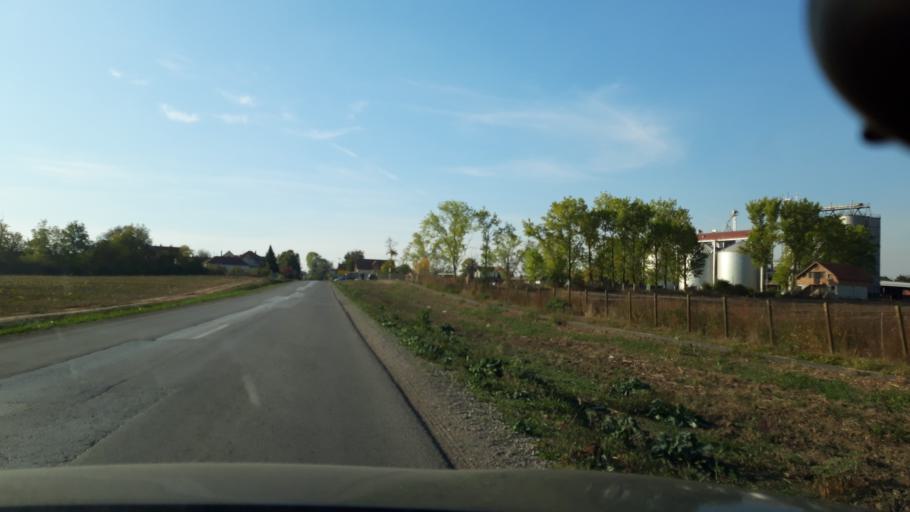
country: RS
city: Putinci
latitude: 45.0000
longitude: 19.9419
